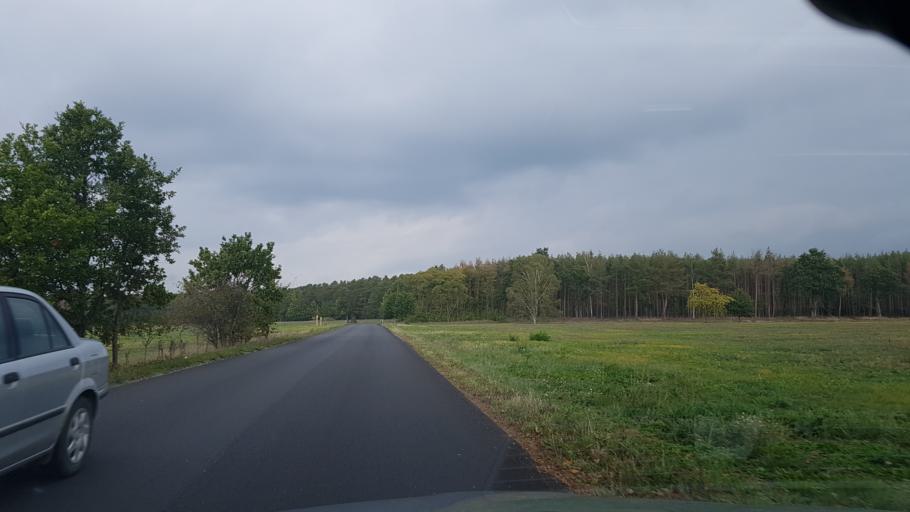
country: DE
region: Brandenburg
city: Elsterwerda
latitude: 51.4714
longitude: 13.4789
